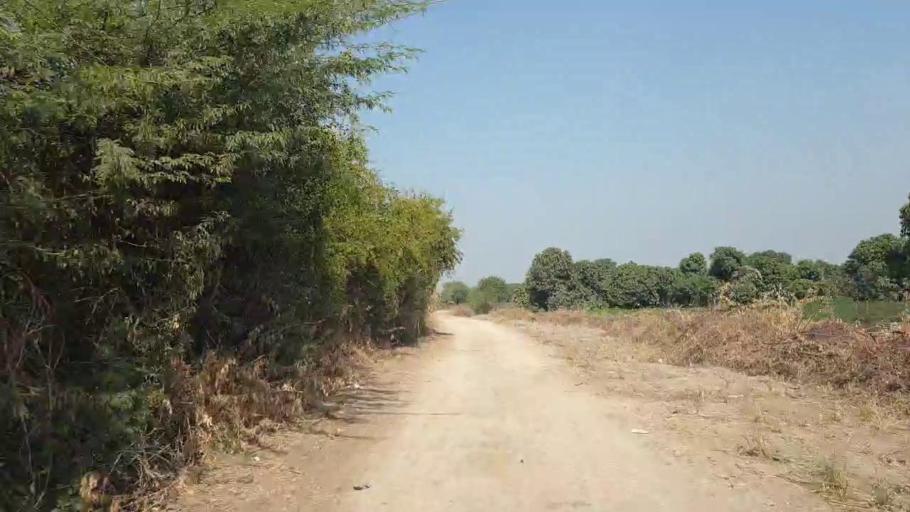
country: PK
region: Sindh
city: Chambar
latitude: 25.4045
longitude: 68.9018
